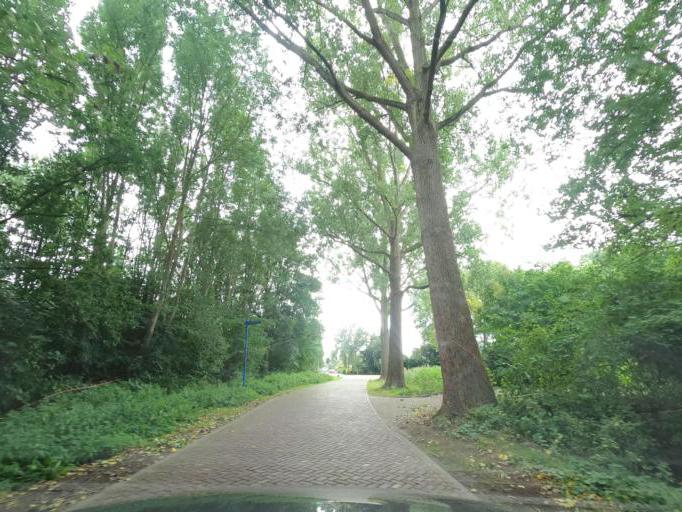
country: NL
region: North Brabant
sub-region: Gemeente Waalwijk
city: Waspik
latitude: 51.6924
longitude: 4.9431
